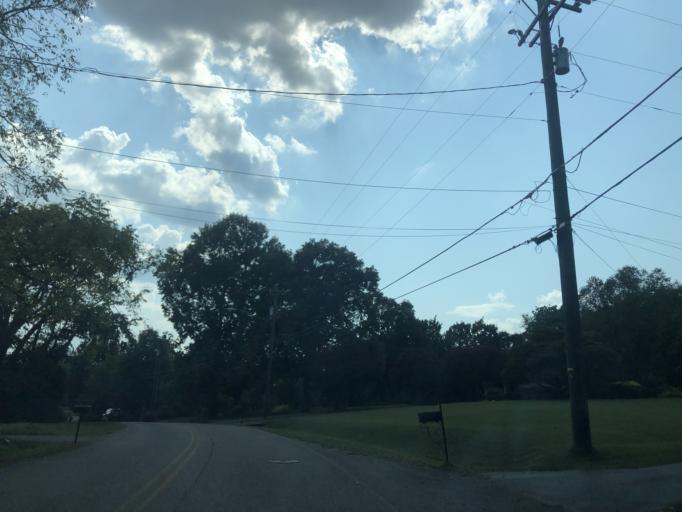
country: US
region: Tennessee
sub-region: Davidson County
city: Oak Hill
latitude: 36.0995
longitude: -86.7803
